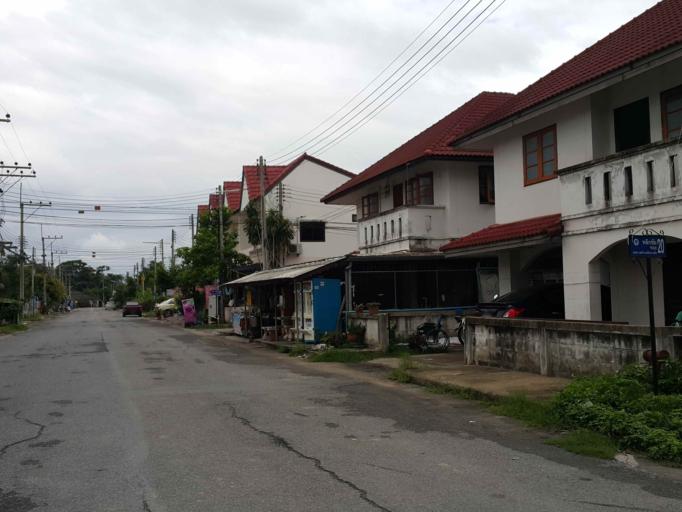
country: TH
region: Chiang Mai
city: San Sai
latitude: 18.8265
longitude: 99.0555
